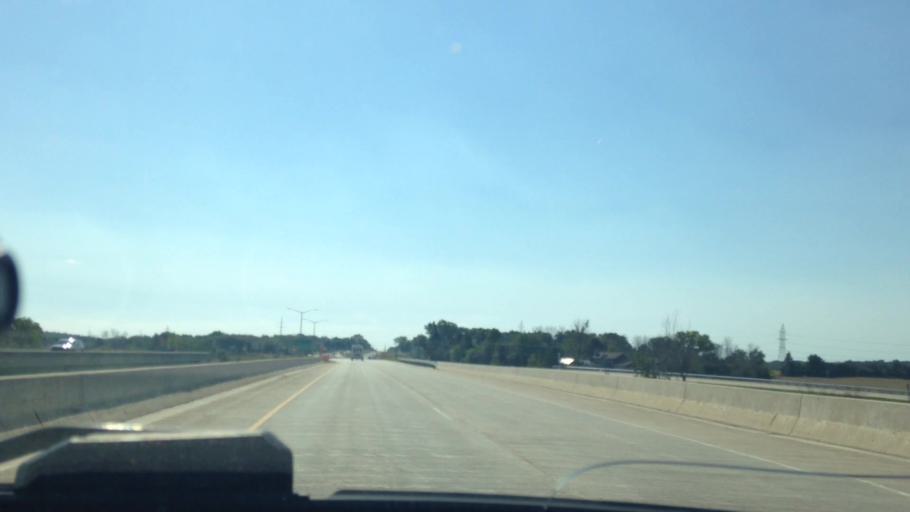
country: US
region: Wisconsin
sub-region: Ozaukee County
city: Grafton
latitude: 43.3391
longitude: -87.9258
